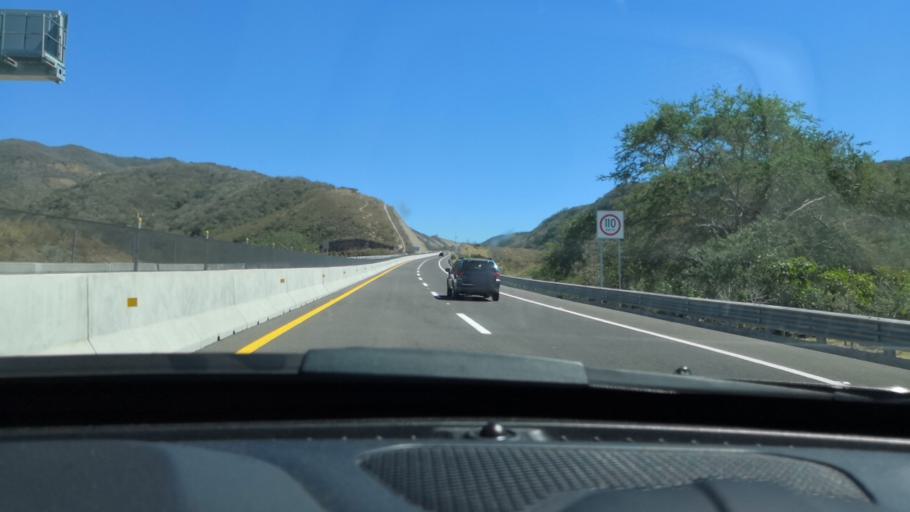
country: MX
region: Nayarit
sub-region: Compostela
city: Juan Escutia (Borbollon)
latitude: 21.1349
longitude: -104.9107
